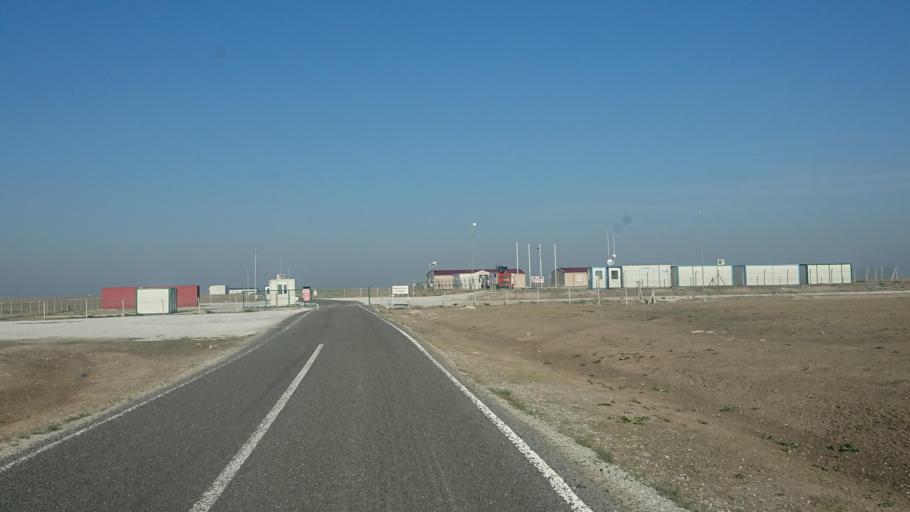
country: TR
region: Aksaray
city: Yesilova
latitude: 38.3881
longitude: 33.7483
